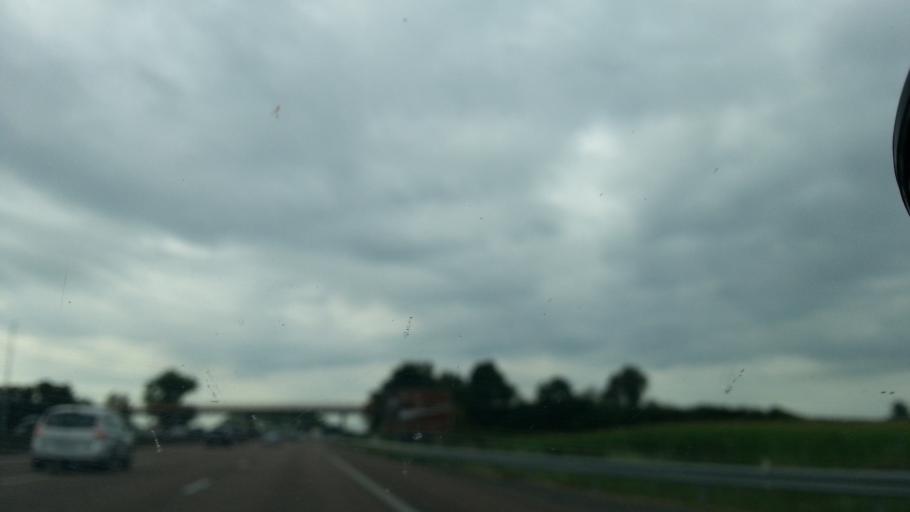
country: FR
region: Bourgogne
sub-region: Departement de Saone-et-Loire
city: Champforgeuil
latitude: 46.8422
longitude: 4.8312
